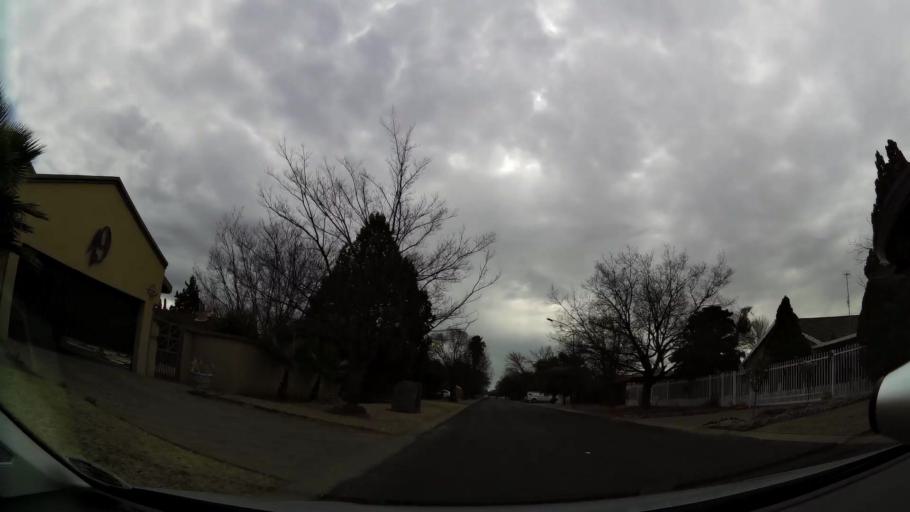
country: ZA
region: Orange Free State
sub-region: Fezile Dabi District Municipality
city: Kroonstad
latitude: -27.6343
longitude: 27.2412
